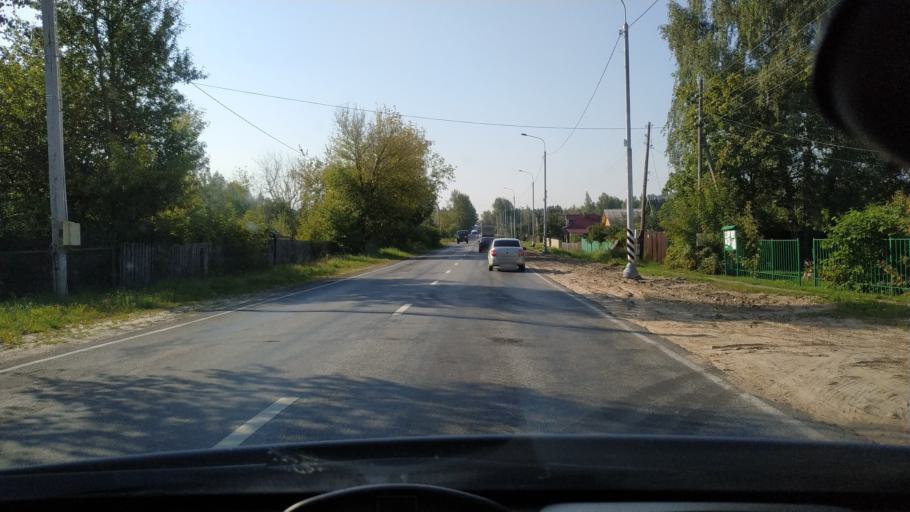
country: RU
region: Moskovskaya
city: Tugolesskiy Bor
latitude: 55.5213
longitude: 39.7111
